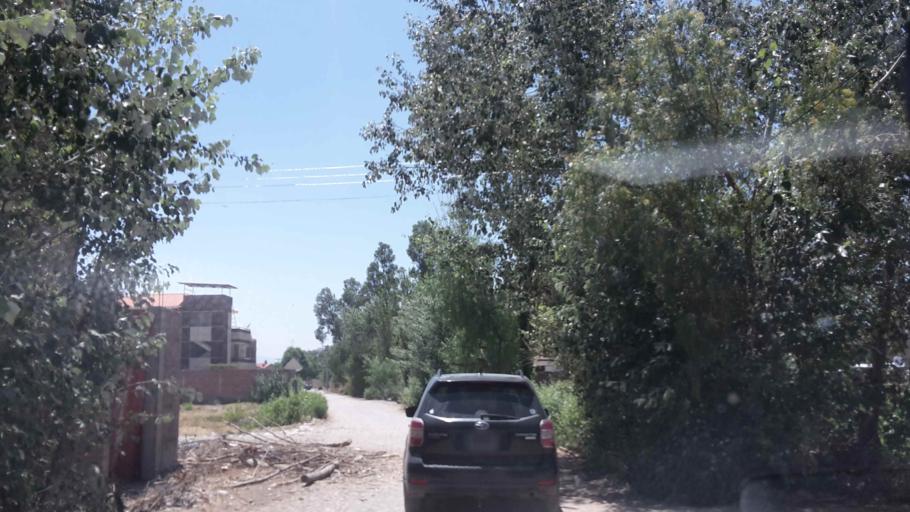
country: BO
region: Cochabamba
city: Cochabamba
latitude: -17.3716
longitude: -66.1956
